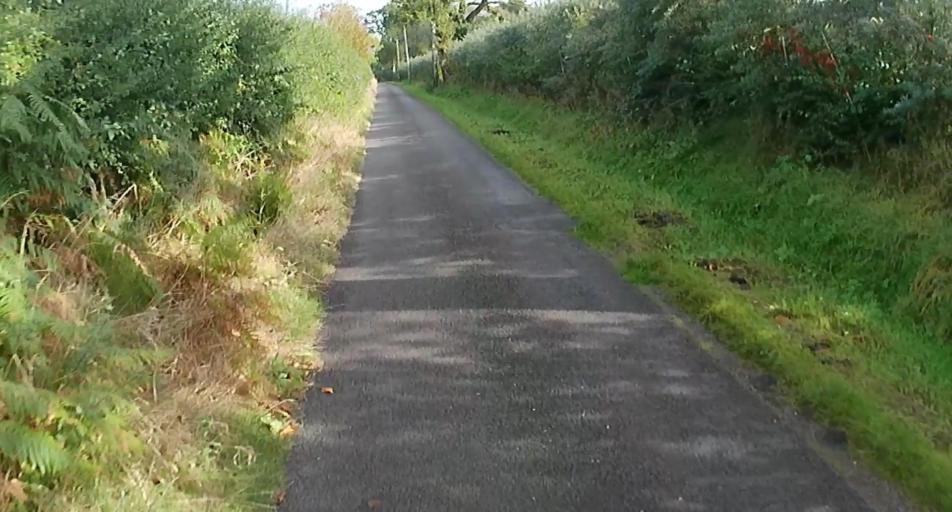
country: GB
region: England
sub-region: Hampshire
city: Tadley
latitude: 51.3116
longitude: -1.1624
